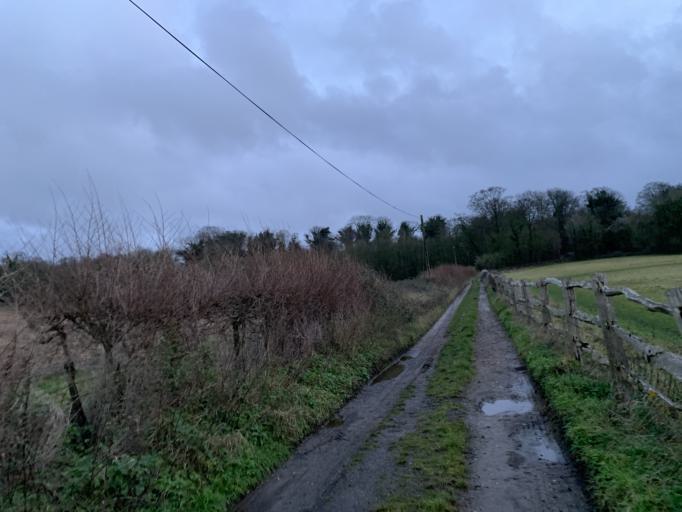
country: GB
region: England
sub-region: Kent
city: Eynsford
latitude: 51.3621
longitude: 0.2004
